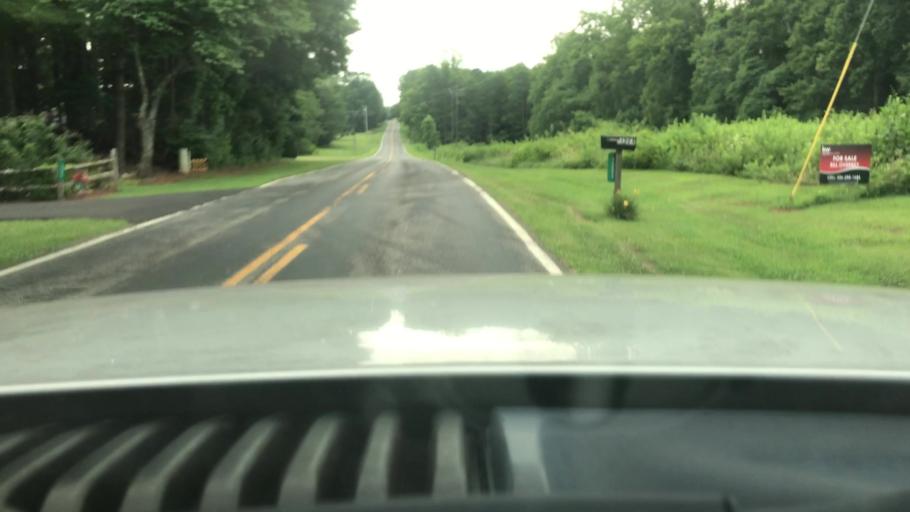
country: US
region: North Carolina
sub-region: Surry County
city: Dobson
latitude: 36.4203
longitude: -80.8302
